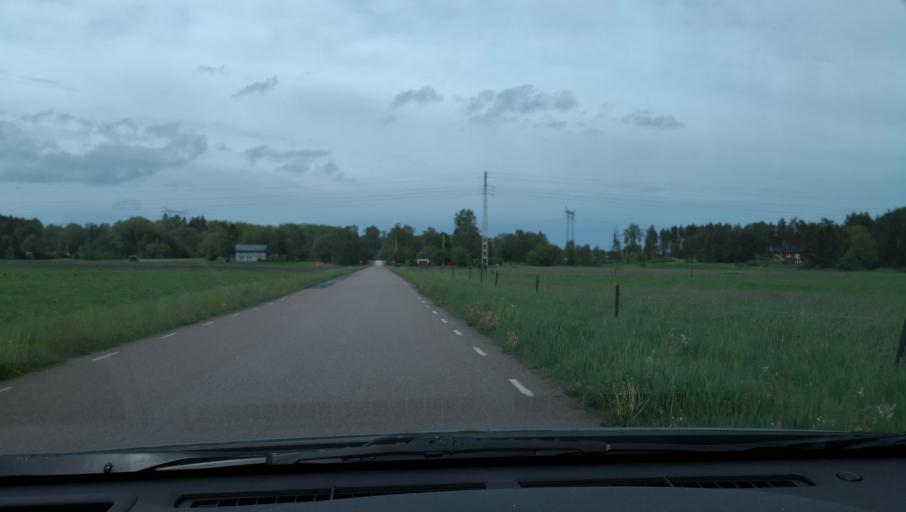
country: SE
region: Uppsala
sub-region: Enkopings Kommun
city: Orsundsbro
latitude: 59.6854
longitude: 17.3795
